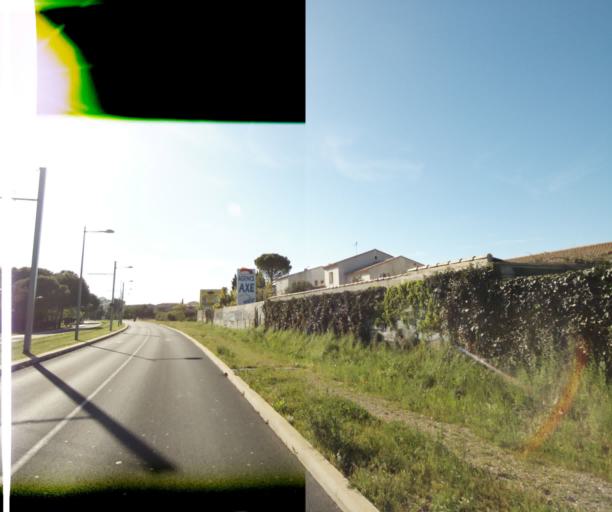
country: FR
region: Languedoc-Roussillon
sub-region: Departement de l'Herault
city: Lattes
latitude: 43.5717
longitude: 3.9115
